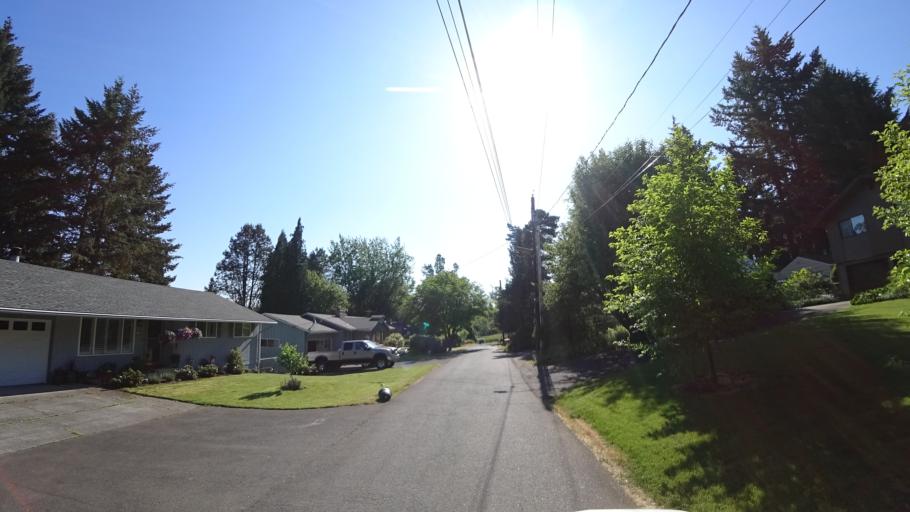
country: US
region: Oregon
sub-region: Clackamas County
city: Happy Valley
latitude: 45.4719
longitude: -122.5360
